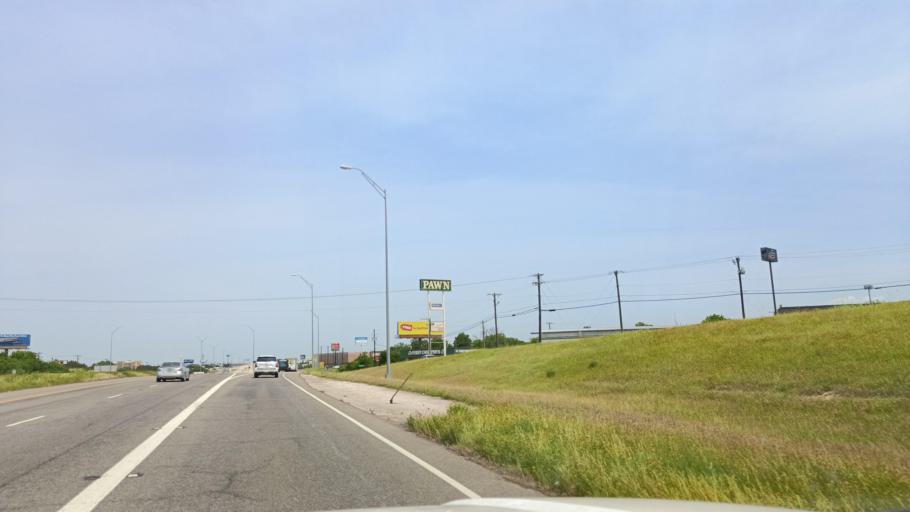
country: US
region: Texas
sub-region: Bell County
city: Temple
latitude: 31.0809
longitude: -97.3826
